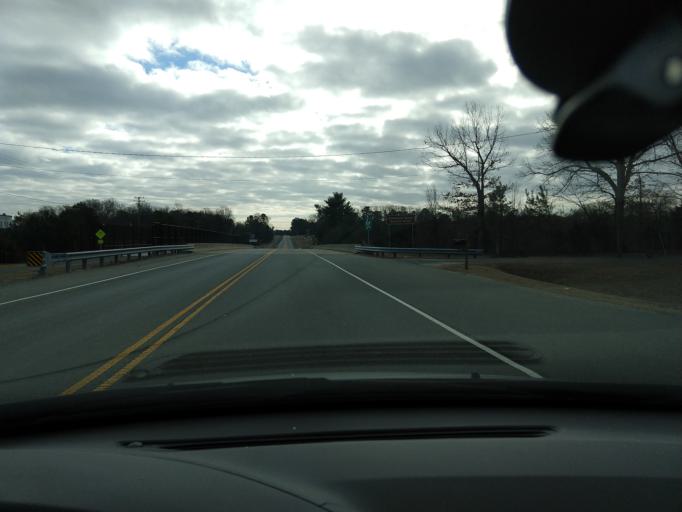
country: US
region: Virginia
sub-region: Henrico County
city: Fort Lee
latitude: 37.4621
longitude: -77.3796
